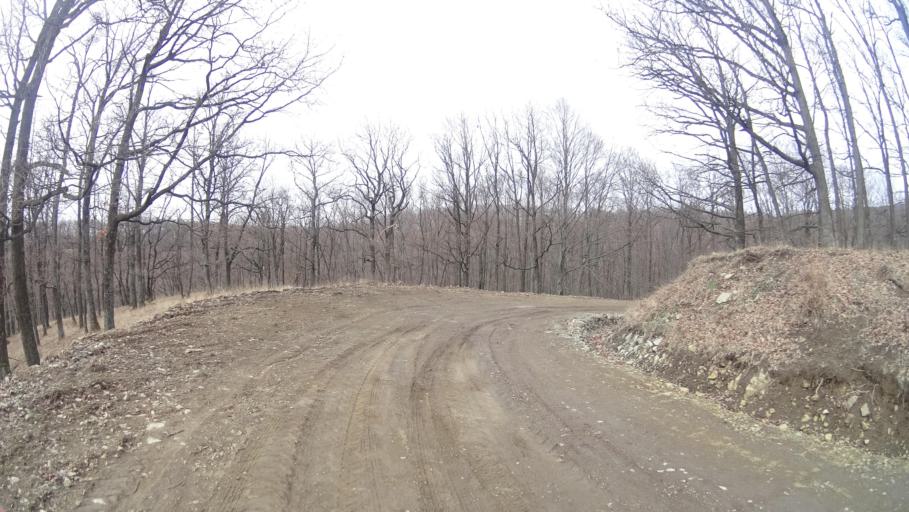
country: HU
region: Pest
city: Szob
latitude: 47.9162
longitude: 18.8959
